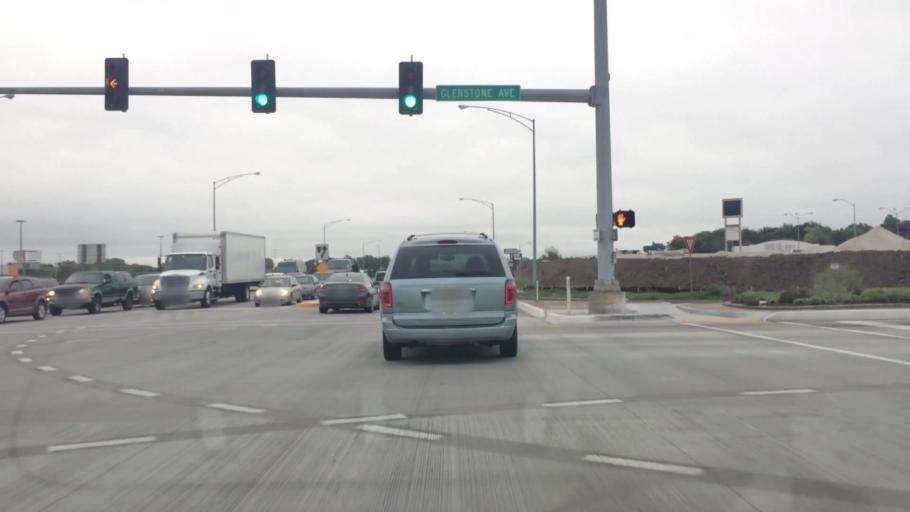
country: US
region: Missouri
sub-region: Greene County
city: Springfield
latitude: 37.2401
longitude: -93.2633
